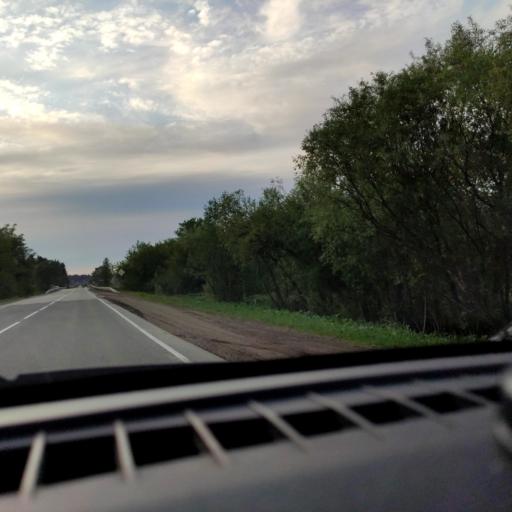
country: RU
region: Perm
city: Ust'-Kachka
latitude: 57.9962
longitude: 55.7104
